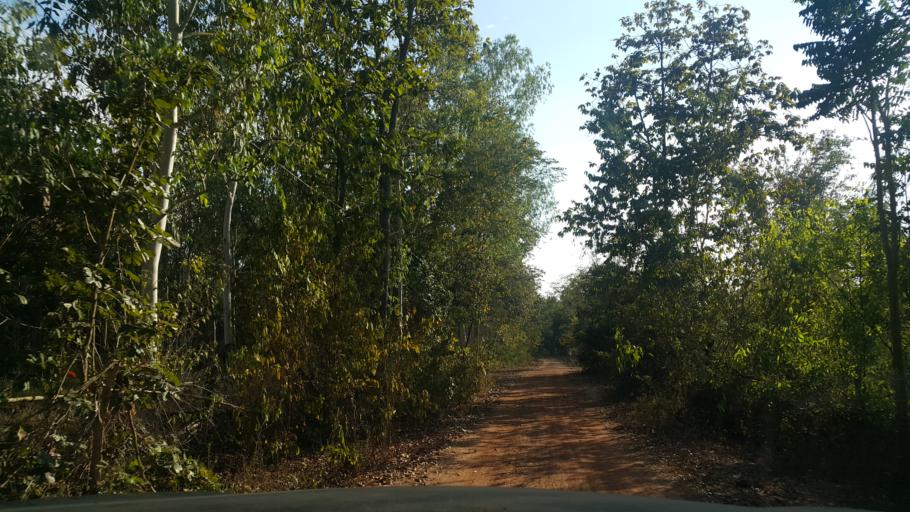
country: TH
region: Lampang
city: Hang Chat
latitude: 18.2910
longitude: 99.3548
